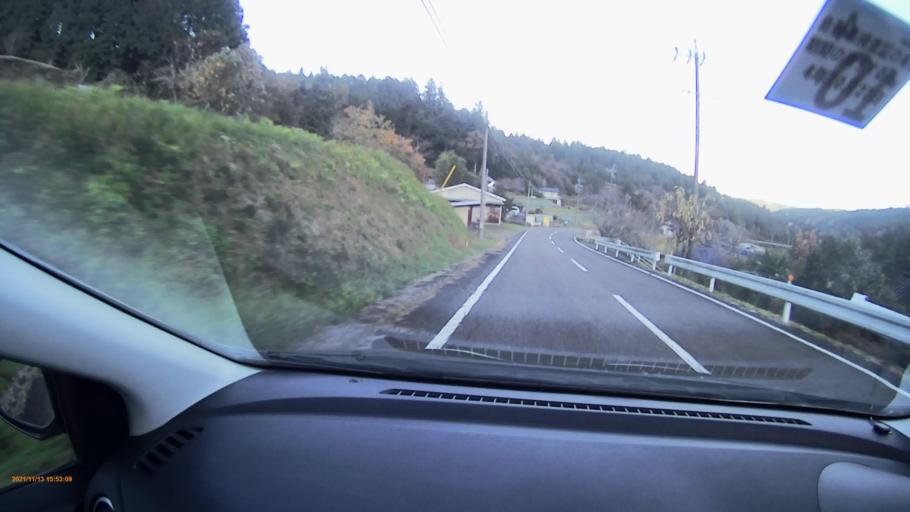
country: JP
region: Gifu
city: Nakatsugawa
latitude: 35.5975
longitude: 137.4352
